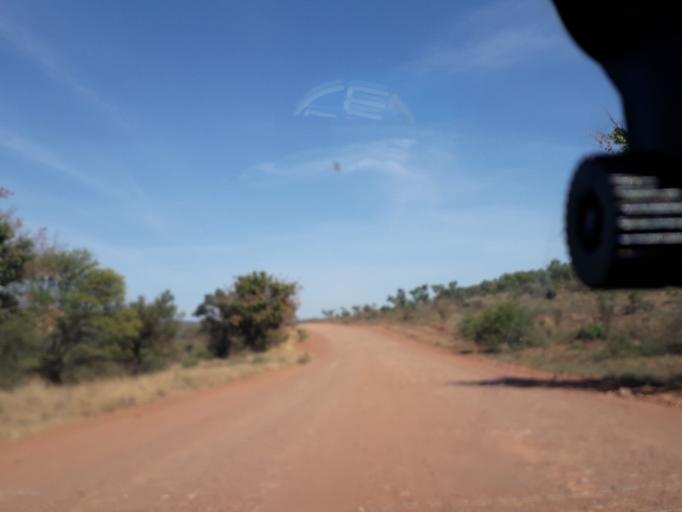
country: ZA
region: Limpopo
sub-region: Waterberg District Municipality
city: Warmbaths
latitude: -24.8259
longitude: 28.2134
